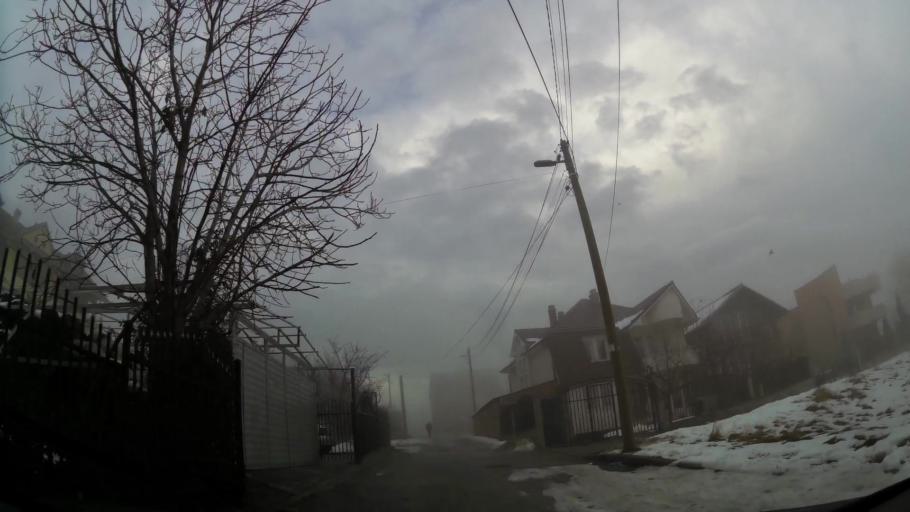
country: XK
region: Pristina
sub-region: Komuna e Prishtines
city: Pristina
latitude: 42.6608
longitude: 21.1452
